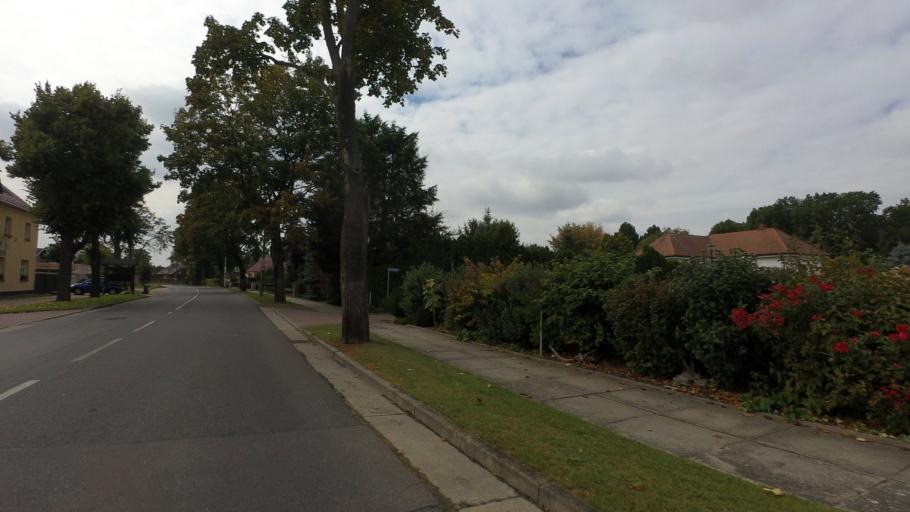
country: DE
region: Brandenburg
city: Luckau
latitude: 51.8412
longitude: 13.6921
